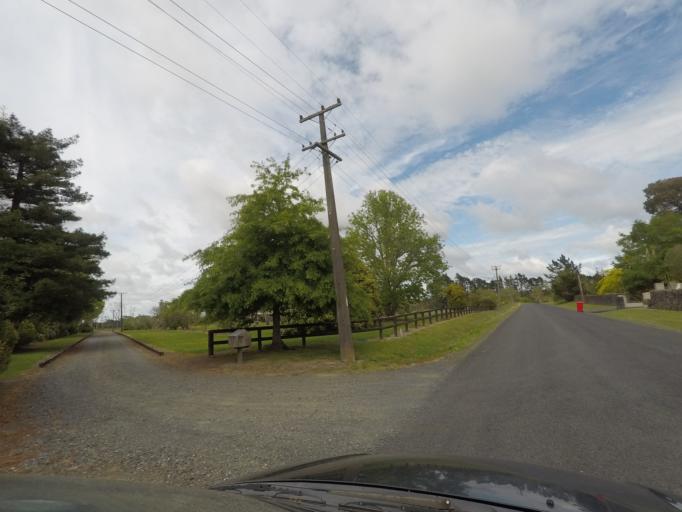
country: NZ
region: Auckland
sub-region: Auckland
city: Rosebank
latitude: -36.7764
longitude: 174.5947
